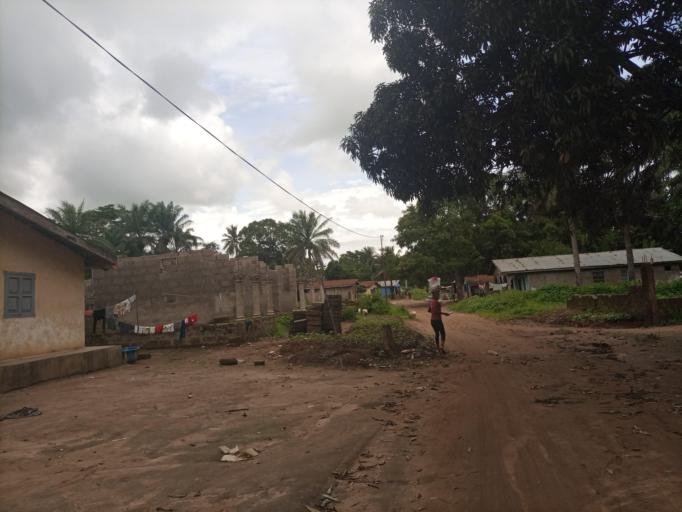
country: SL
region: Northern Province
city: Masoyila
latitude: 8.5909
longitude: -13.1650
